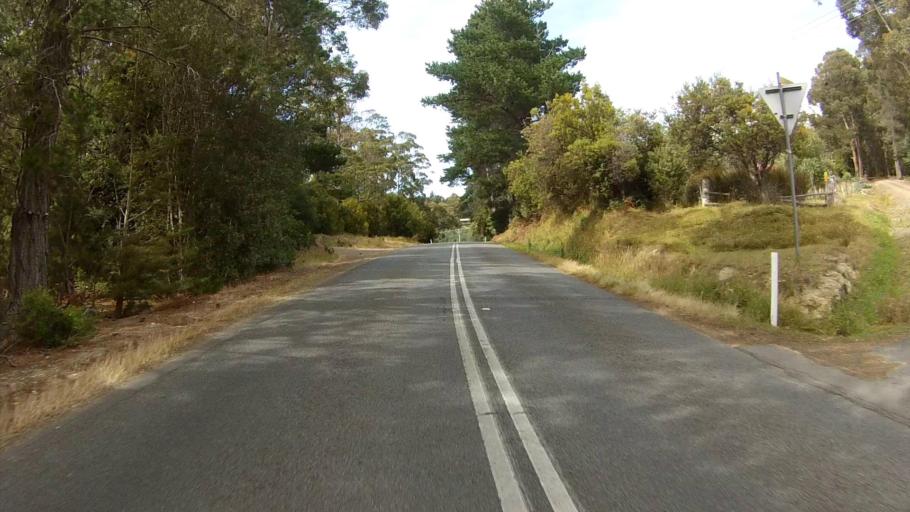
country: AU
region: Tasmania
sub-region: Kingborough
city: Kettering
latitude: -43.1892
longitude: 147.2452
